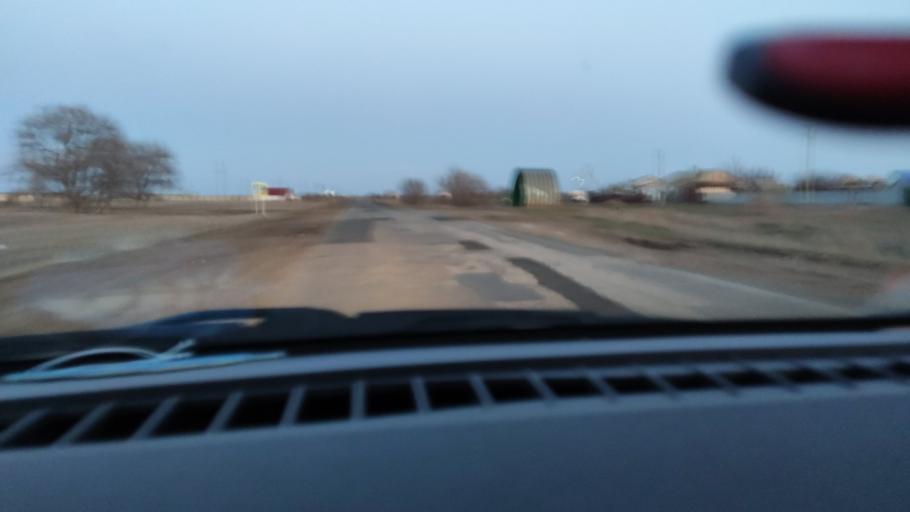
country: RU
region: Saratov
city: Rovnoye
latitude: 51.0590
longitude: 46.0263
